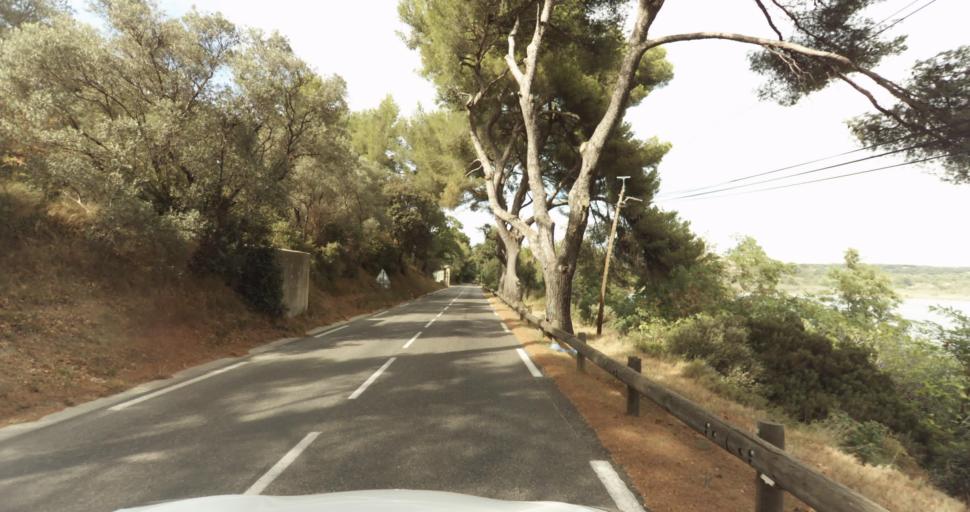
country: FR
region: Provence-Alpes-Cote d'Azur
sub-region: Departement des Bouches-du-Rhone
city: Saint-Chamas
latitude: 43.5534
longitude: 5.0121
